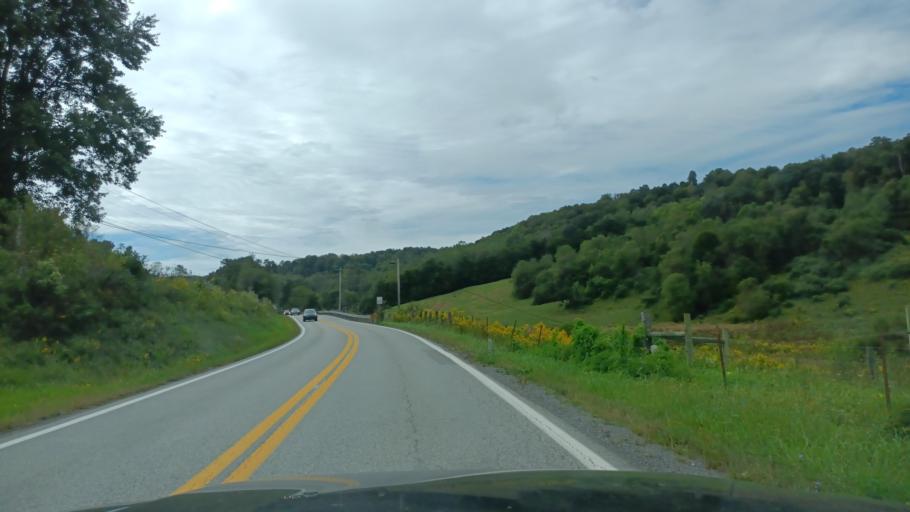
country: US
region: West Virginia
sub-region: Taylor County
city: Grafton
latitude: 39.3296
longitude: -80.1092
